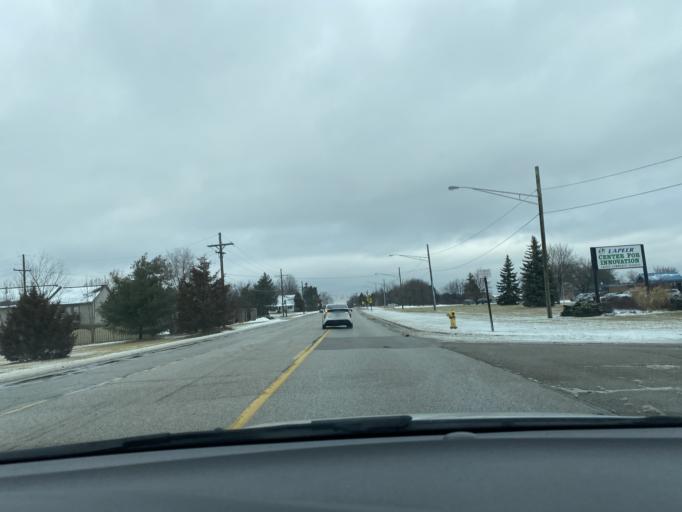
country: US
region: Michigan
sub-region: Lapeer County
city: Lapeer
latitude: 43.0548
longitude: -83.3427
